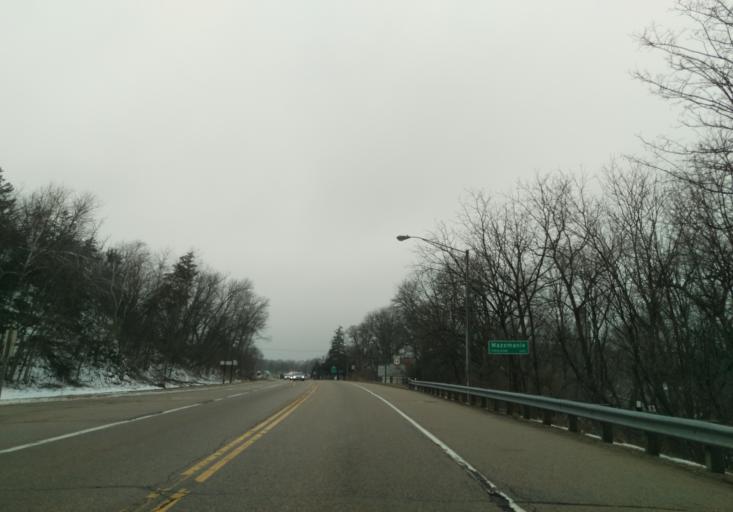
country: US
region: Wisconsin
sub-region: Dane County
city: Mazomanie
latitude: 43.1725
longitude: -89.7891
